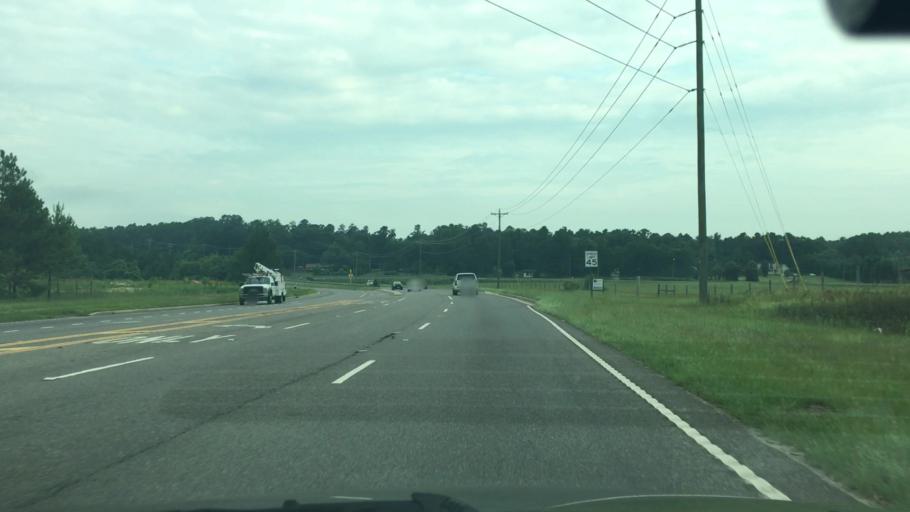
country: US
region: South Carolina
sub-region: Aiken County
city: Aiken
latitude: 33.5683
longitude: -81.6891
